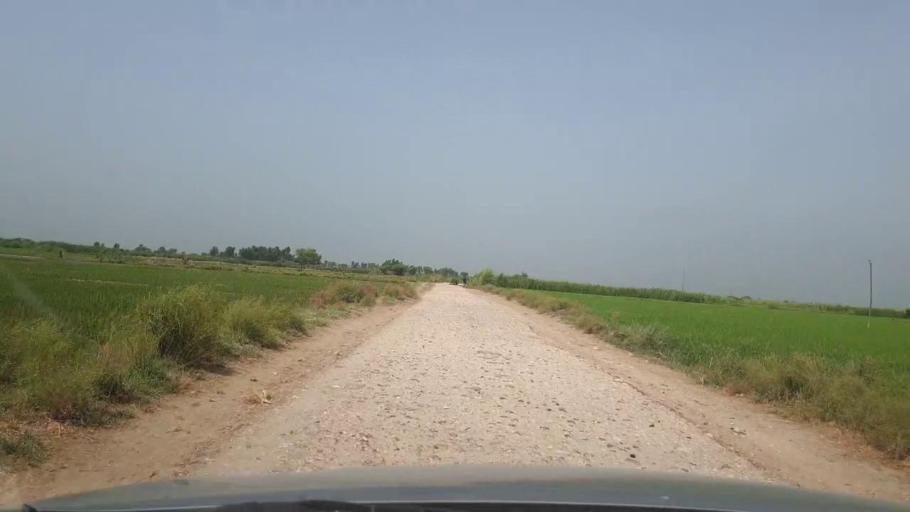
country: PK
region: Sindh
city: Garhi Yasin
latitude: 27.9084
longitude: 68.3931
